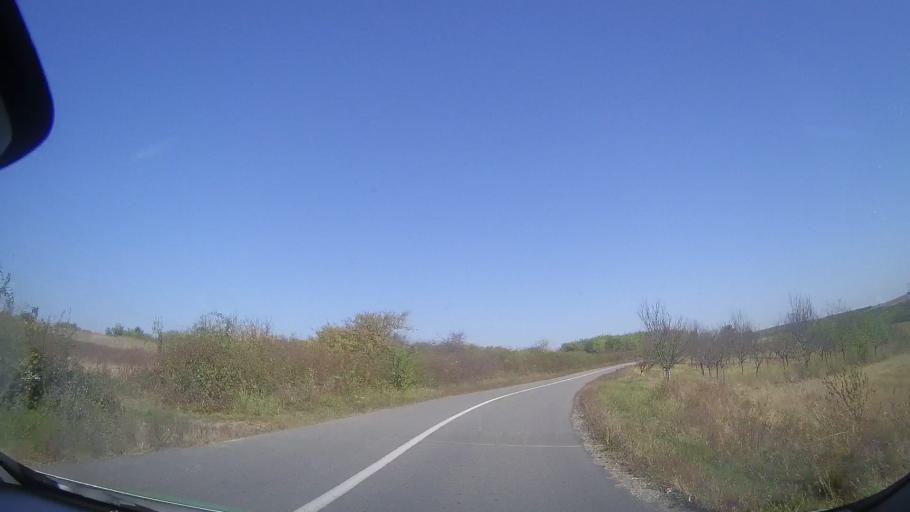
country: RO
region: Timis
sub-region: Comuna Balint
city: Balint
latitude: 45.8244
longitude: 21.8495
